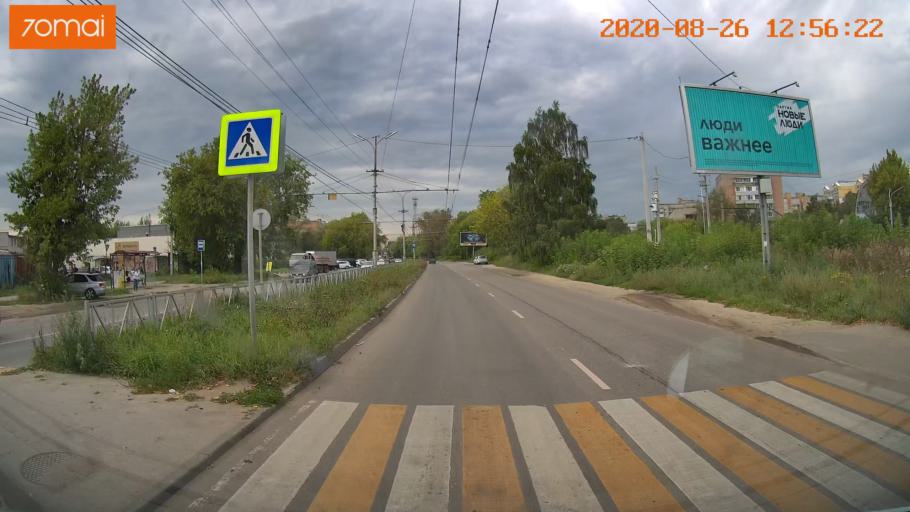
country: RU
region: Rjazan
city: Ryazan'
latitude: 54.6132
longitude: 39.7513
